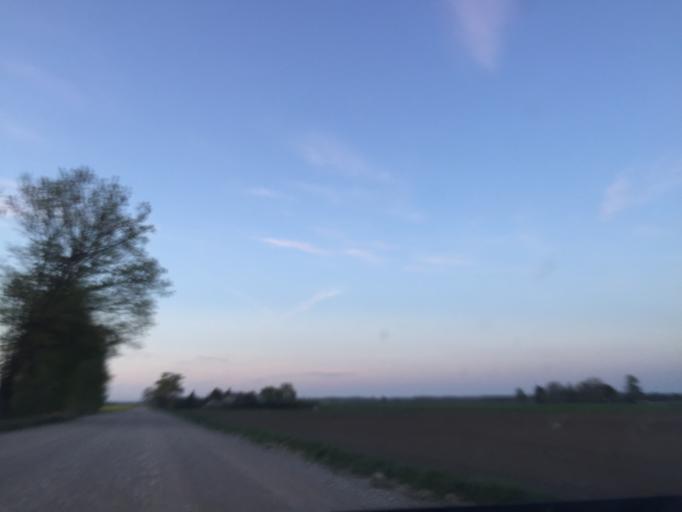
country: LV
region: Rundales
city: Pilsrundale
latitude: 56.4551
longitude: 24.0667
